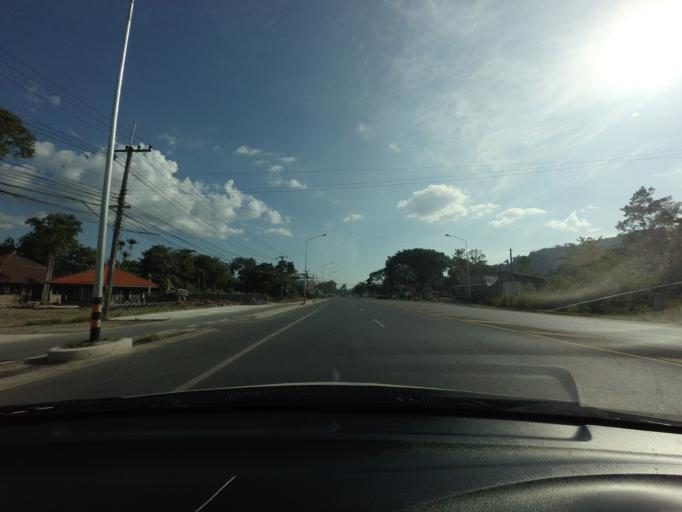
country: TH
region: Nakhon Nayok
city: Nakhon Nayok
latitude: 14.3066
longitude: 101.2934
